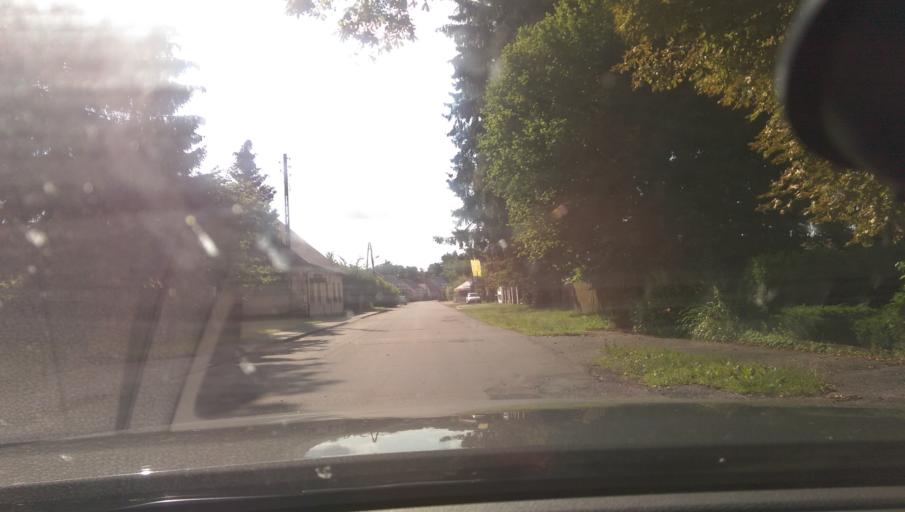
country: PL
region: West Pomeranian Voivodeship
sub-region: Powiat walecki
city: Walcz
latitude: 53.3801
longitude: 16.4987
